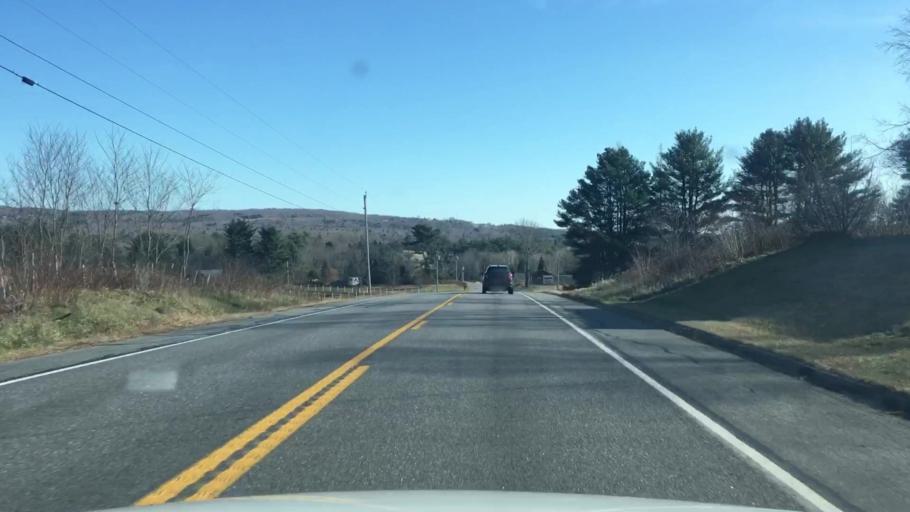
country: US
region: Maine
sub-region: Knox County
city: Washington
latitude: 44.2411
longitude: -69.3701
